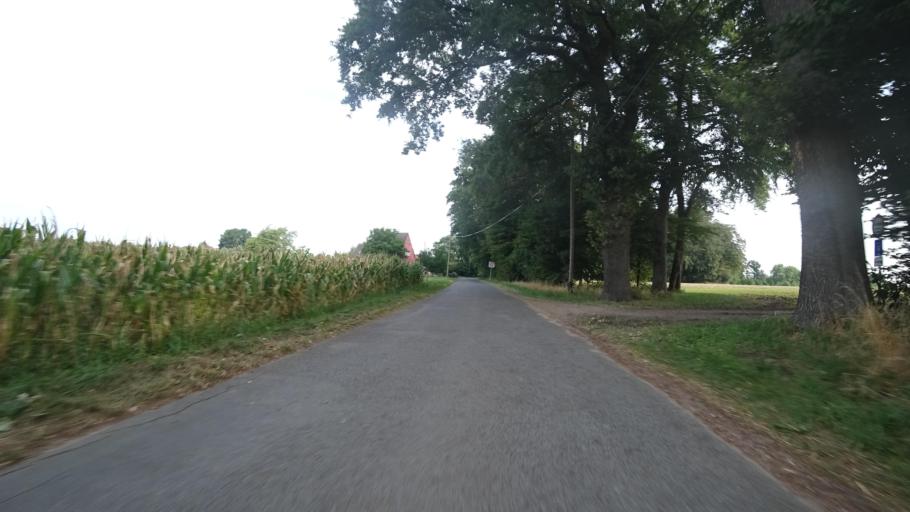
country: DE
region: North Rhine-Westphalia
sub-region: Regierungsbezirk Detmold
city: Steinhagen
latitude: 51.9566
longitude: 8.4558
